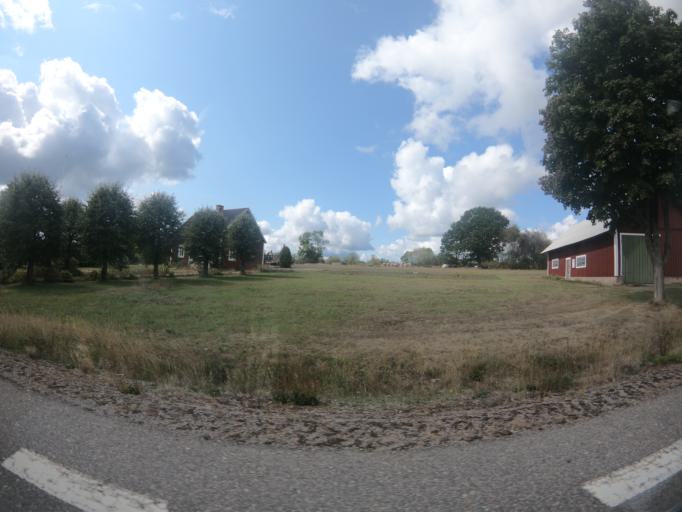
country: SE
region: Kronoberg
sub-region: Vaxjo Kommun
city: Braas
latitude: 57.1102
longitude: 14.9788
